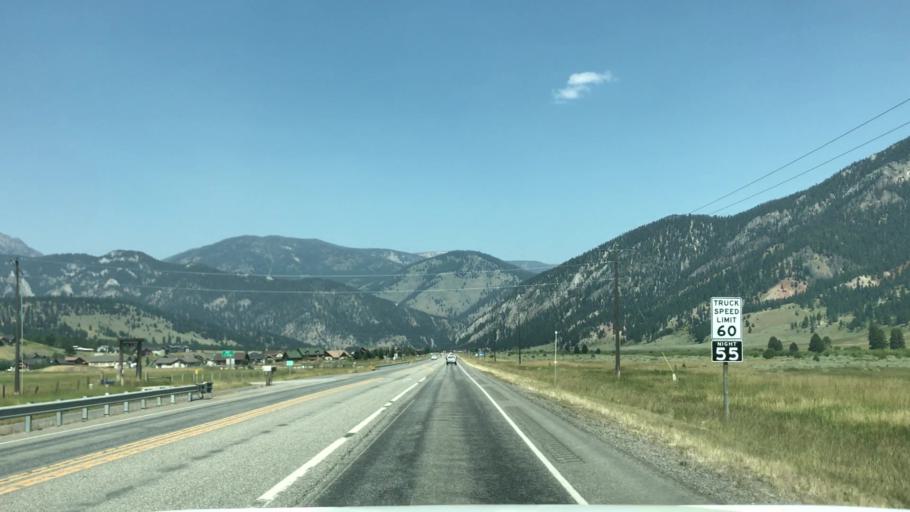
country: US
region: Montana
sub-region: Gallatin County
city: Big Sky
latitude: 45.2345
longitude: -111.2508
